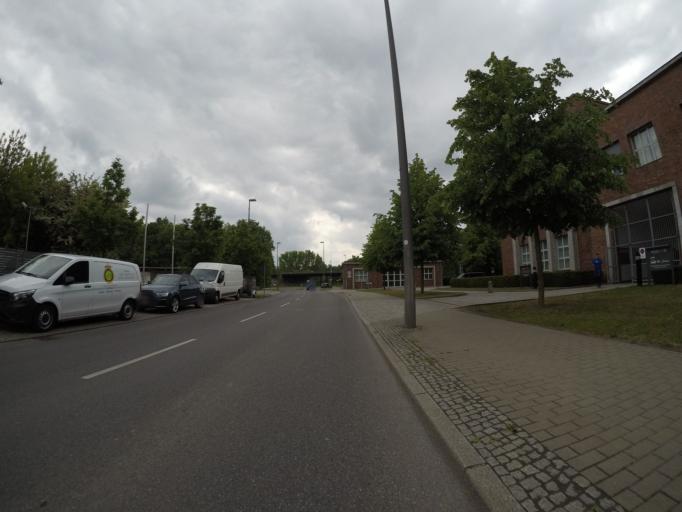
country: DE
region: Berlin
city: Falkenberg
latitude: 52.5413
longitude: 13.5370
